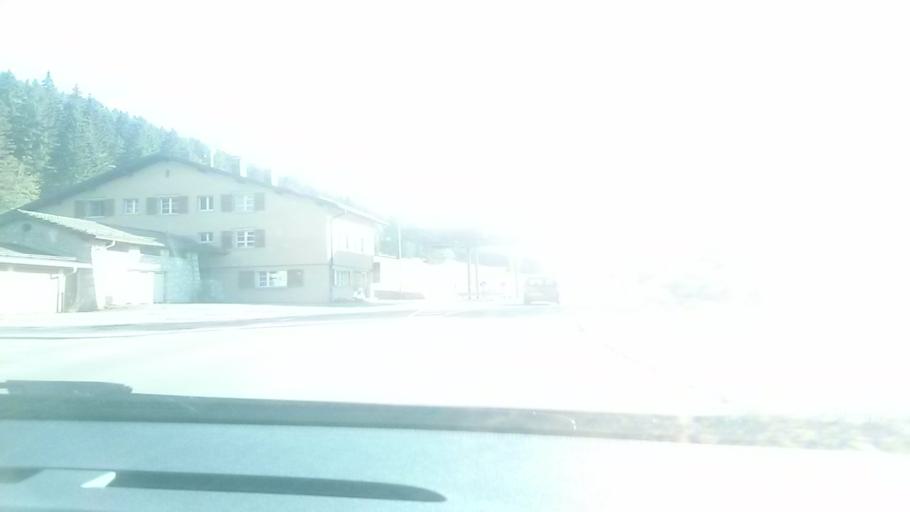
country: CH
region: Vaud
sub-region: Jura-Nord vaudois District
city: Le Chenit
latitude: 46.5489
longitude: 6.1594
